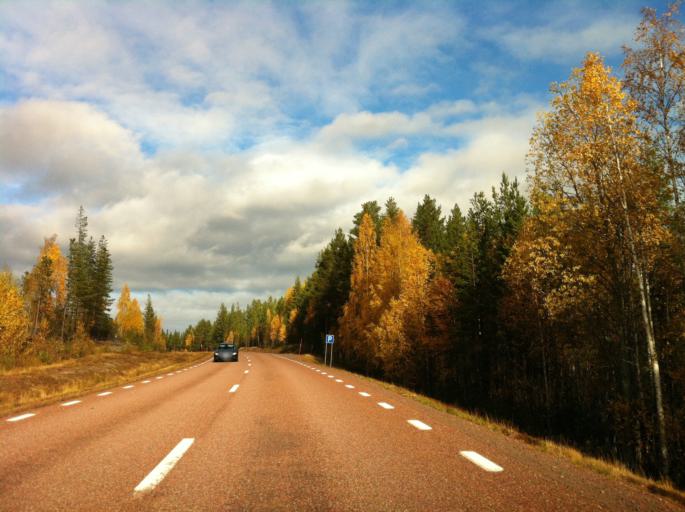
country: SE
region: Dalarna
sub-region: Alvdalens Kommun
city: AElvdalen
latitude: 61.5086
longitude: 13.3800
